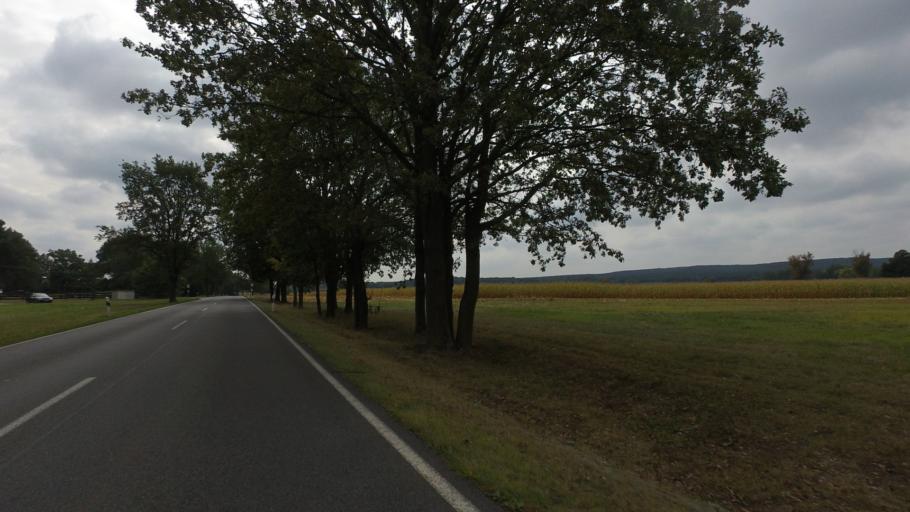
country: DE
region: Brandenburg
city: Luckau
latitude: 51.7815
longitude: 13.6883
